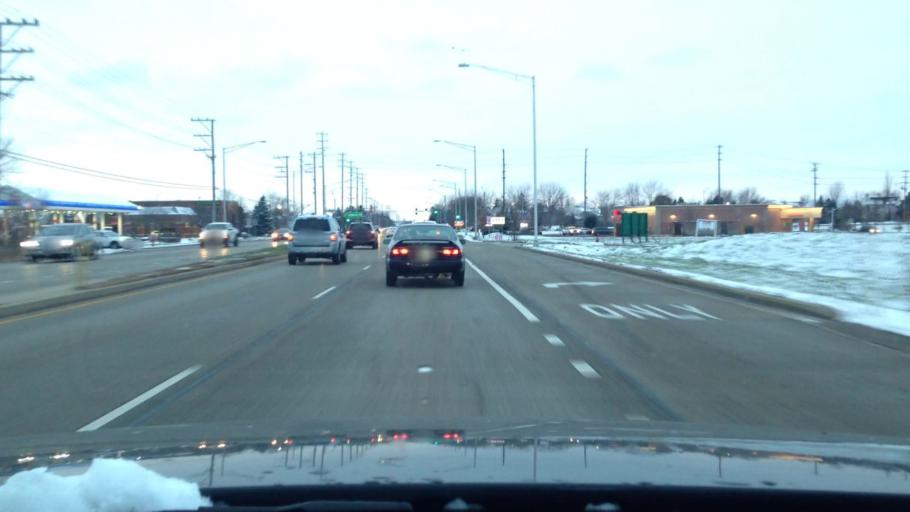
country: US
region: Illinois
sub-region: McHenry County
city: Huntley
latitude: 42.1758
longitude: -88.3802
